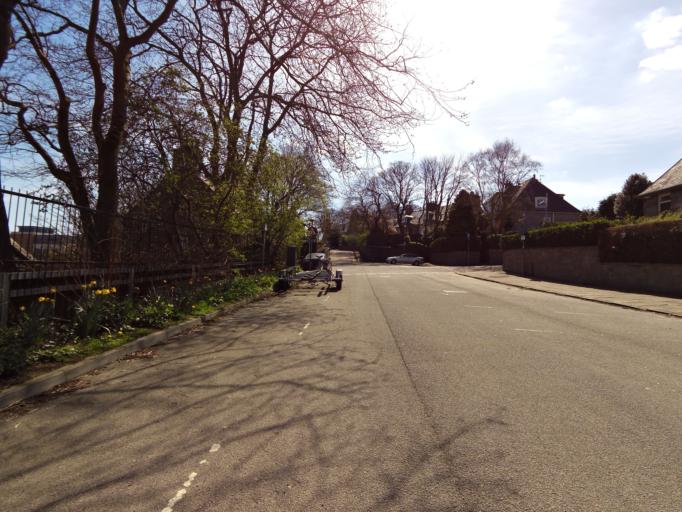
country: GB
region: Scotland
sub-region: Aberdeen City
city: Aberdeen
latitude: 57.1365
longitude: -2.0989
